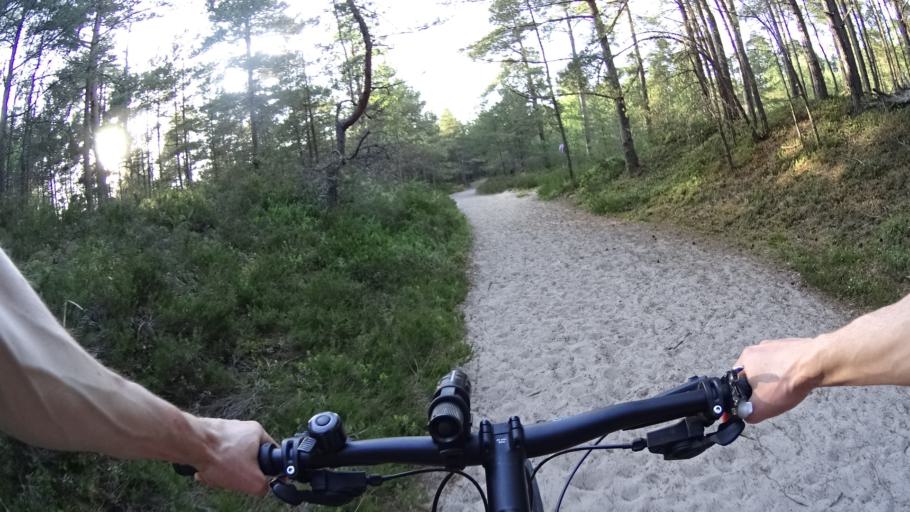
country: LV
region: Riga
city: Jaunciems
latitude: 57.0945
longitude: 24.1571
